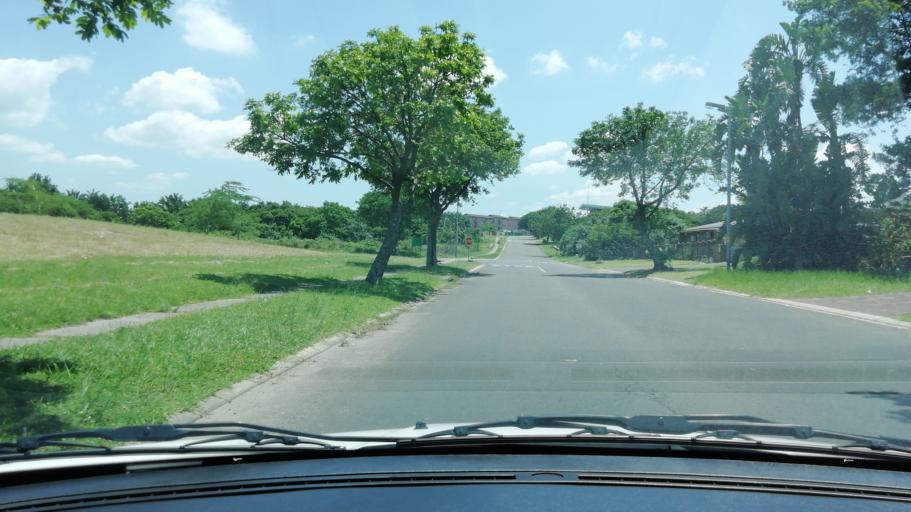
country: ZA
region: KwaZulu-Natal
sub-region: uThungulu District Municipality
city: Richards Bay
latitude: -28.7342
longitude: 32.0501
